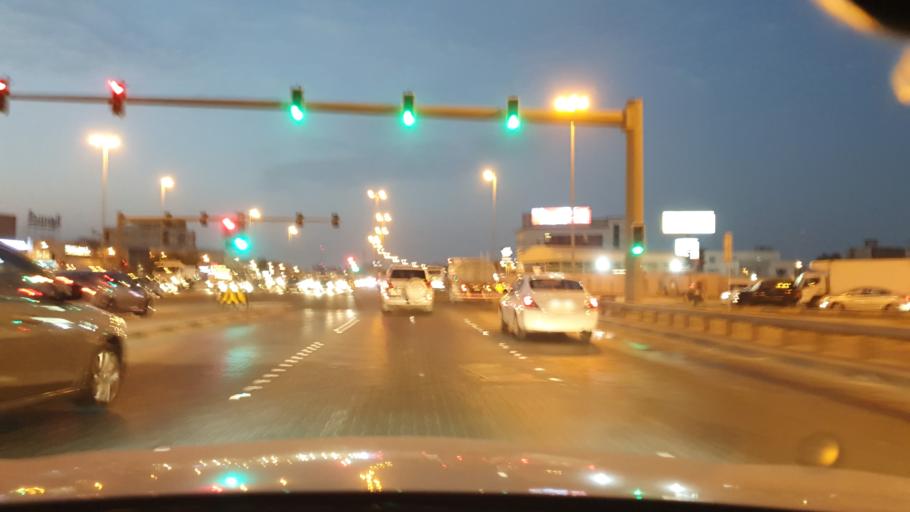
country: BH
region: Northern
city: Ar Rifa'
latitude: 26.1405
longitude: 50.5812
